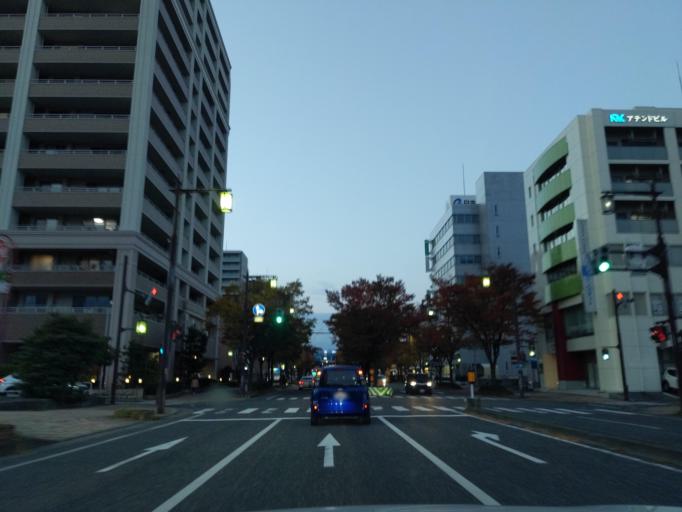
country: JP
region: Niigata
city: Niigata-shi
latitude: 37.9069
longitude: 139.0639
